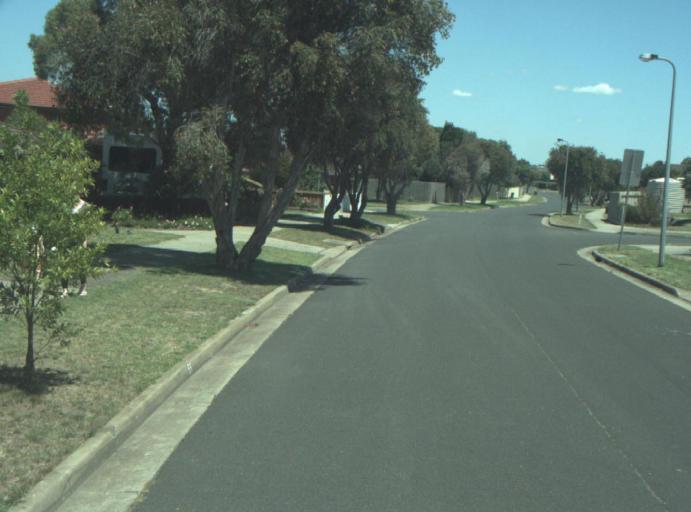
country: AU
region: Victoria
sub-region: Greater Geelong
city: Wandana Heights
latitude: -38.2117
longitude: 144.3256
